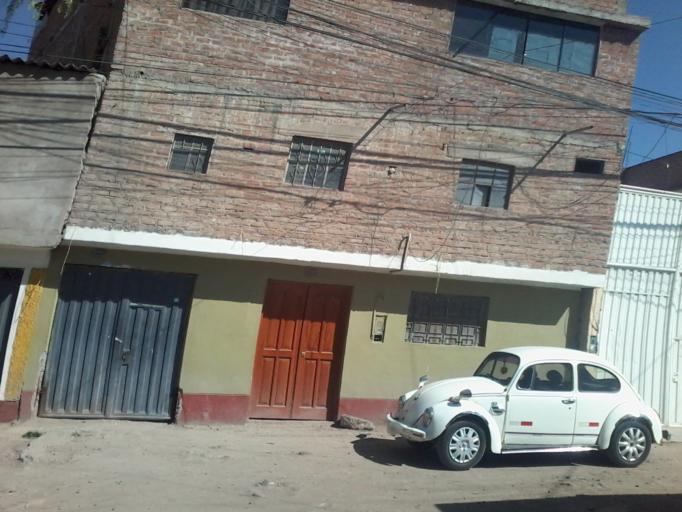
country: PE
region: Ayacucho
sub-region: Provincia de Huamanga
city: Ayacucho
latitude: -13.1584
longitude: -74.2076
